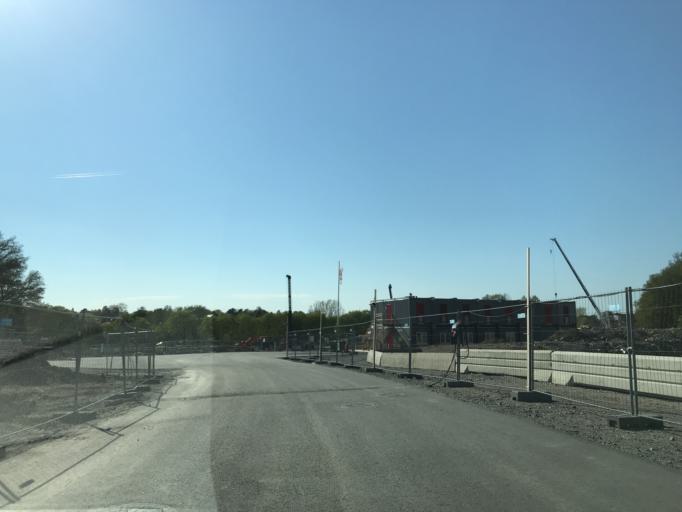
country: SE
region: Stockholm
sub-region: Huddinge Kommun
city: Huddinge
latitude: 59.2825
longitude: 18.0013
